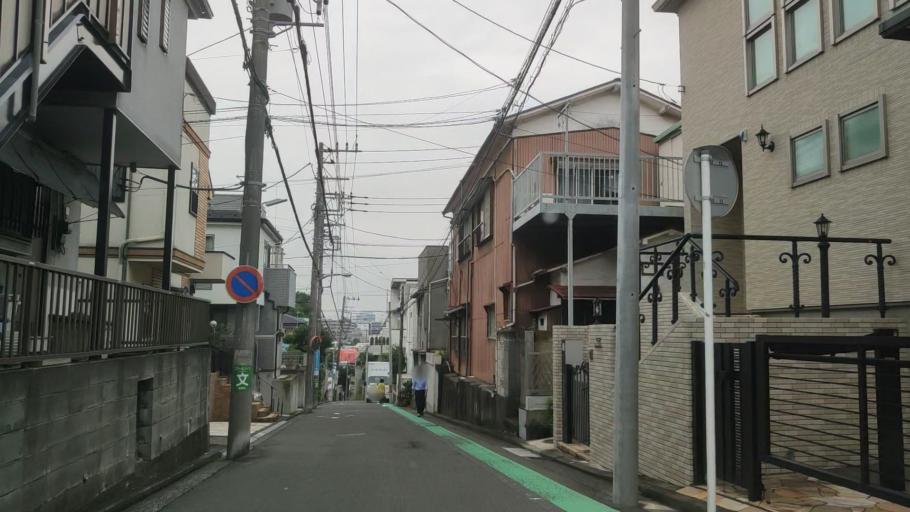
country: JP
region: Kanagawa
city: Yokohama
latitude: 35.4503
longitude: 139.6162
